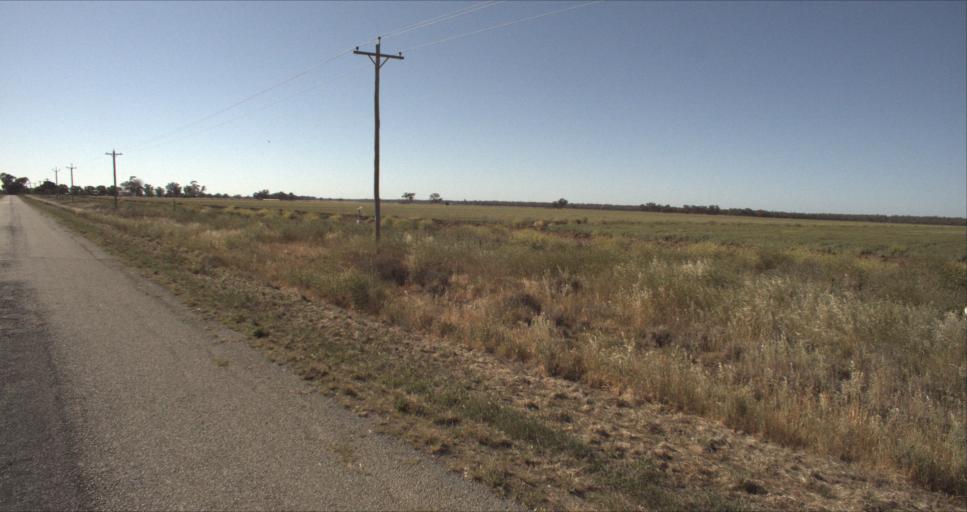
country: AU
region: New South Wales
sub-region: Leeton
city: Leeton
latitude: -34.5827
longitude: 146.3030
